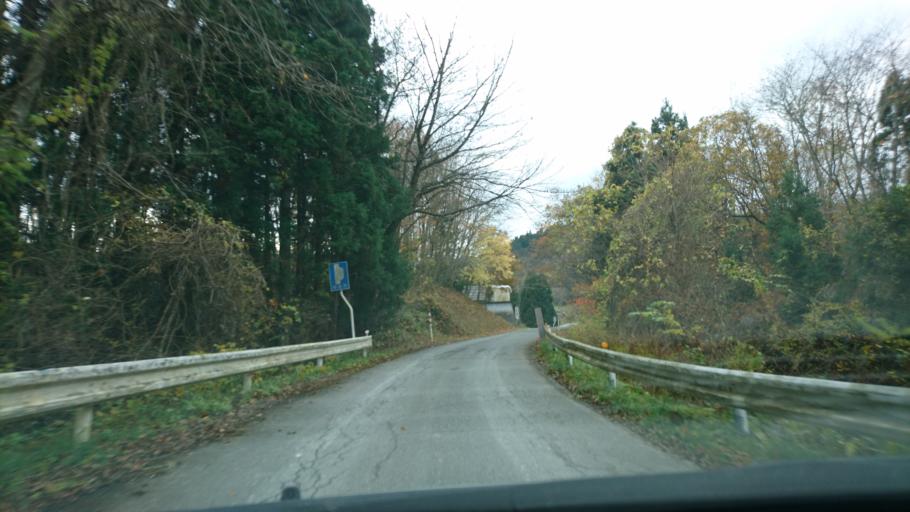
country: JP
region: Iwate
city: Ichinoseki
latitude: 39.0088
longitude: 141.2165
